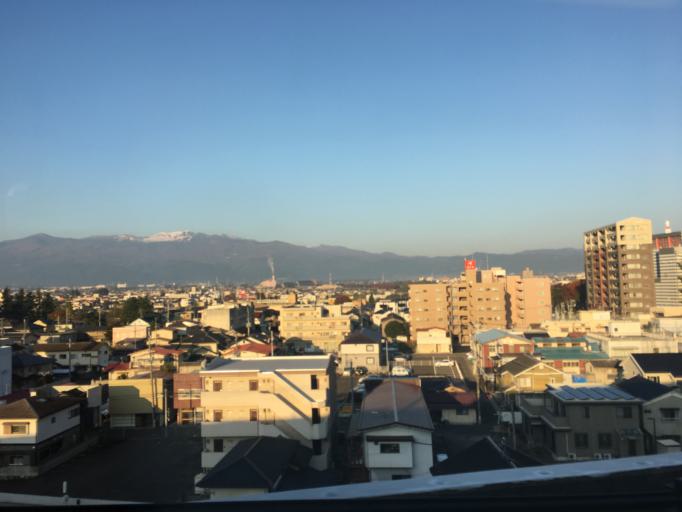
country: JP
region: Fukushima
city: Fukushima-shi
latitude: 37.7510
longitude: 140.4586
